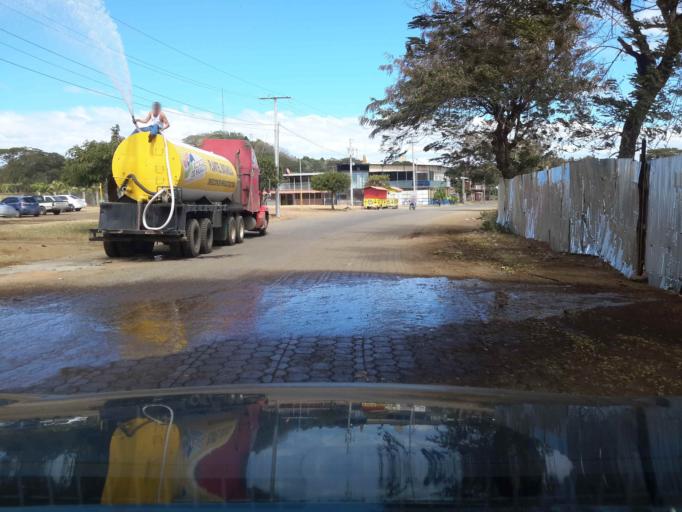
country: NI
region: Managua
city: Managua
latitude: 12.1333
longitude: -86.2718
